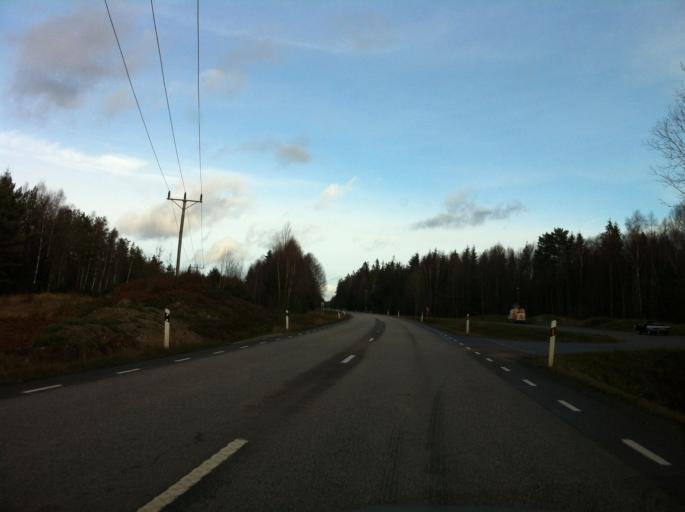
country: SE
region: Kronoberg
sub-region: Almhults Kommun
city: AElmhult
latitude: 56.5769
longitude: 14.1868
